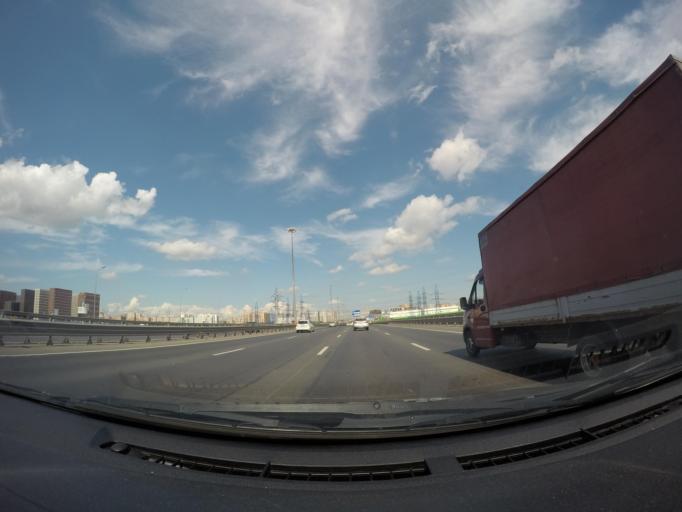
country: RU
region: Moskovskaya
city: Lyubertsy
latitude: 55.6614
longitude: 37.8883
